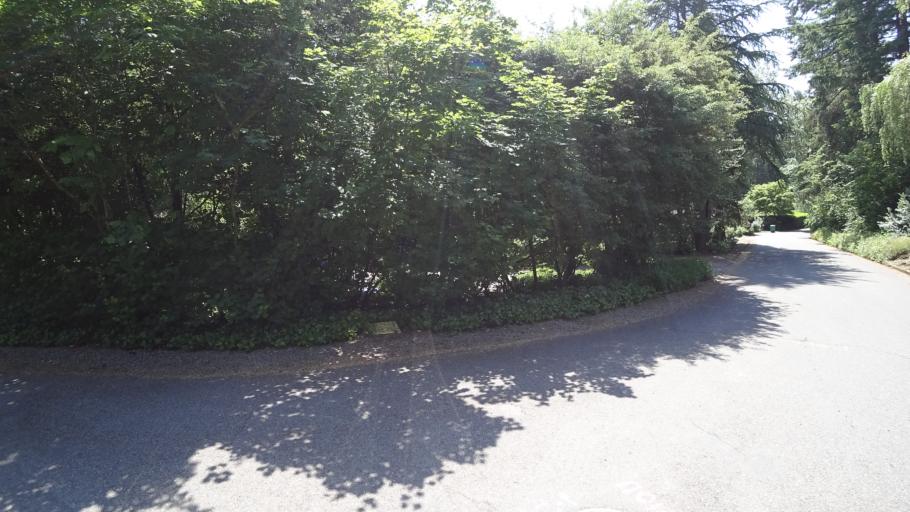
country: US
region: Oregon
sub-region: Washington County
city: West Slope
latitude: 45.5150
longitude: -122.7249
